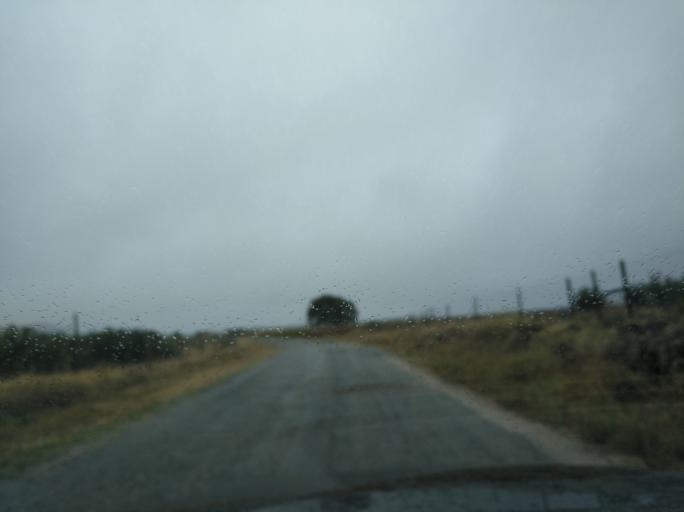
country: PT
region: Portalegre
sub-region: Campo Maior
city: Campo Maior
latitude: 38.9756
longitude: -7.0807
